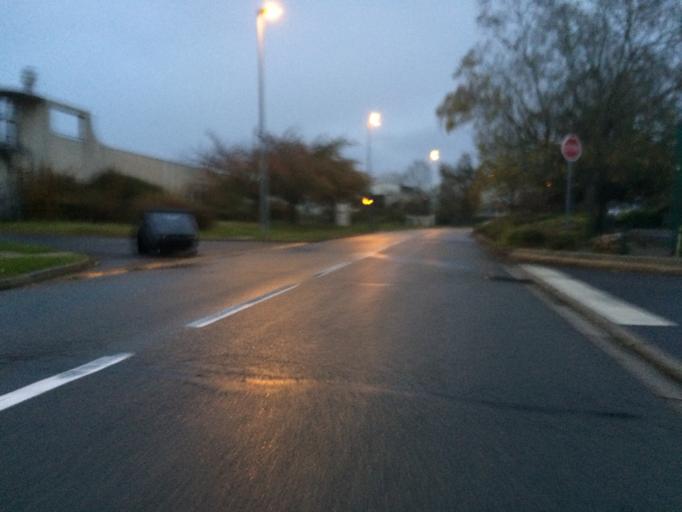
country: FR
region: Ile-de-France
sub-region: Departement de l'Essonne
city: Orsay
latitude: 48.6881
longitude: 2.2109
